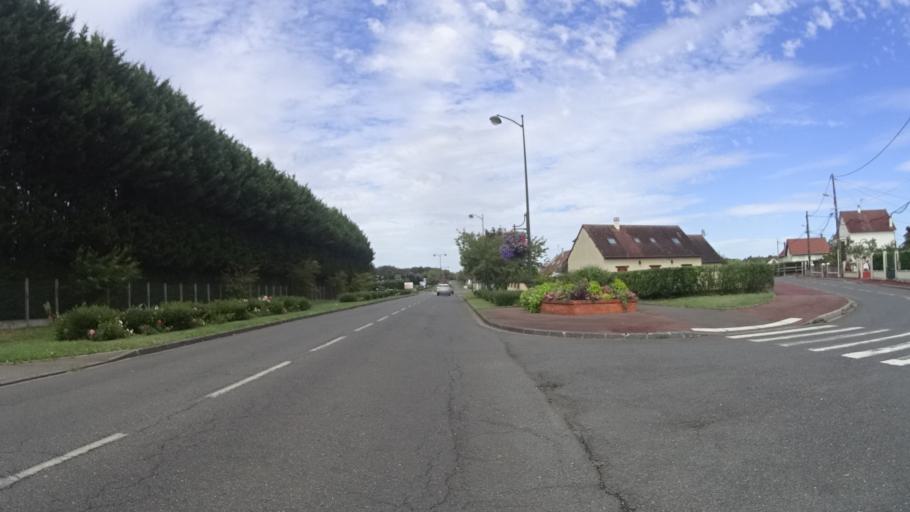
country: FR
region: Centre
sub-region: Departement du Loiret
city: Briare
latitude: 47.6510
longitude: 2.7361
